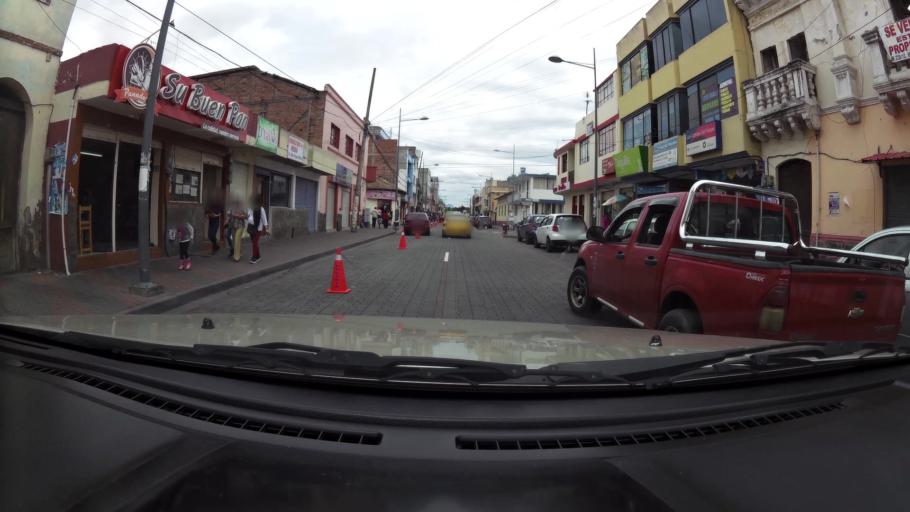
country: EC
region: Cotopaxi
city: San Miguel de Salcedo
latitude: -1.0374
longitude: -78.5908
